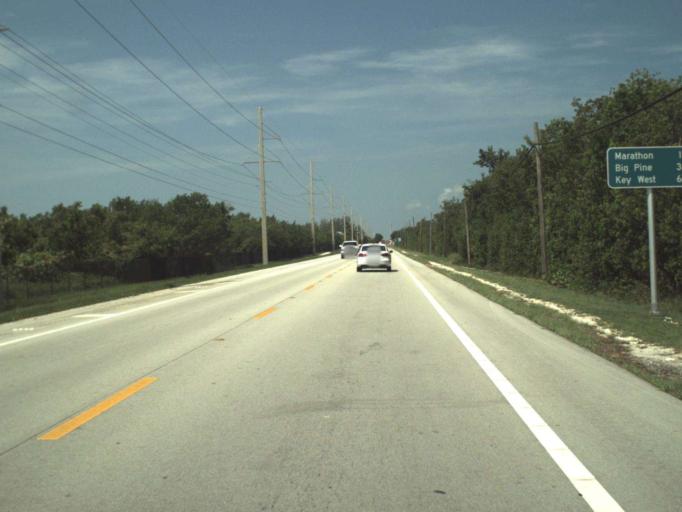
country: US
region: Florida
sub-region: Monroe County
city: Islamorada
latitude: 24.8081
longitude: -80.8366
